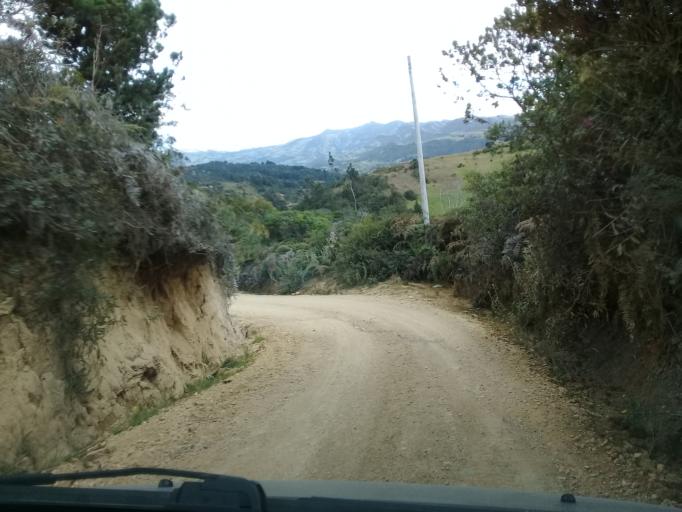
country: CO
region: Cundinamarca
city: Lenguazaque
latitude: 5.2864
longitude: -73.7358
